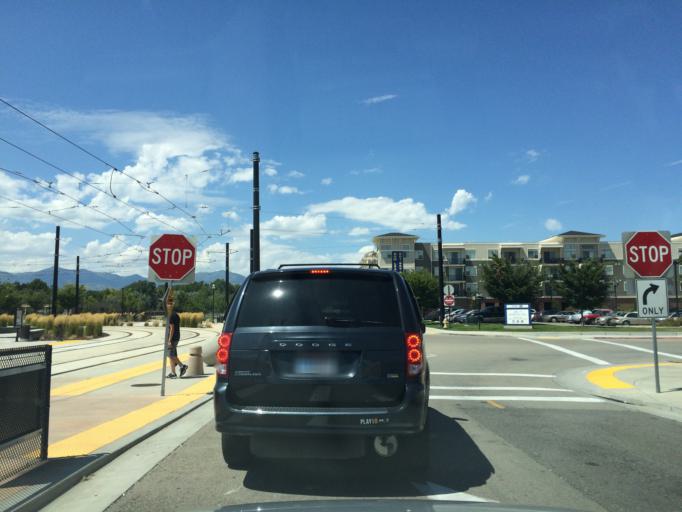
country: US
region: Utah
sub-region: Salt Lake County
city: Taylorsville
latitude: 40.6945
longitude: -111.9600
